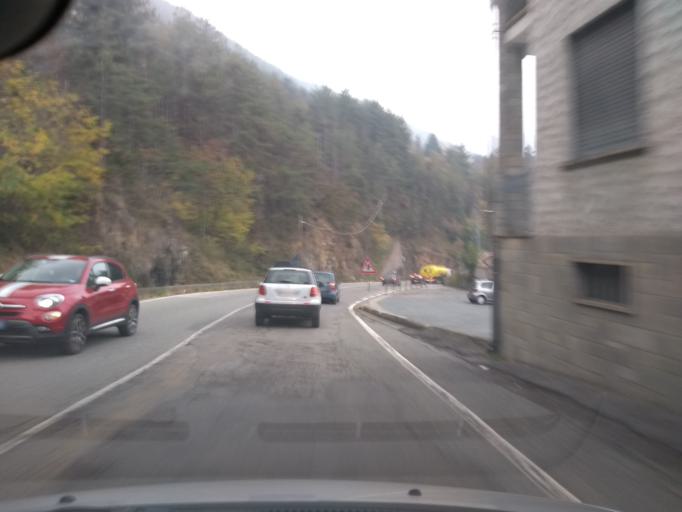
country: IT
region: Piedmont
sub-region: Provincia di Torino
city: Germagnano
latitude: 45.2709
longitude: 7.4528
